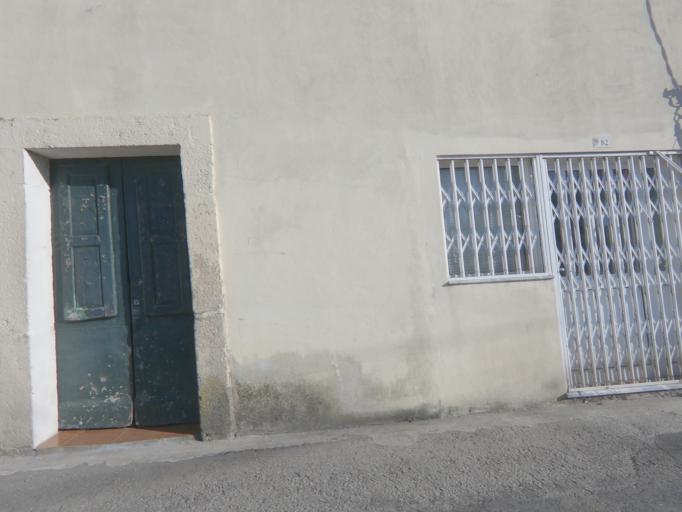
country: PT
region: Vila Real
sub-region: Peso da Regua
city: Peso da Regua
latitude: 41.1875
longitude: -7.7755
